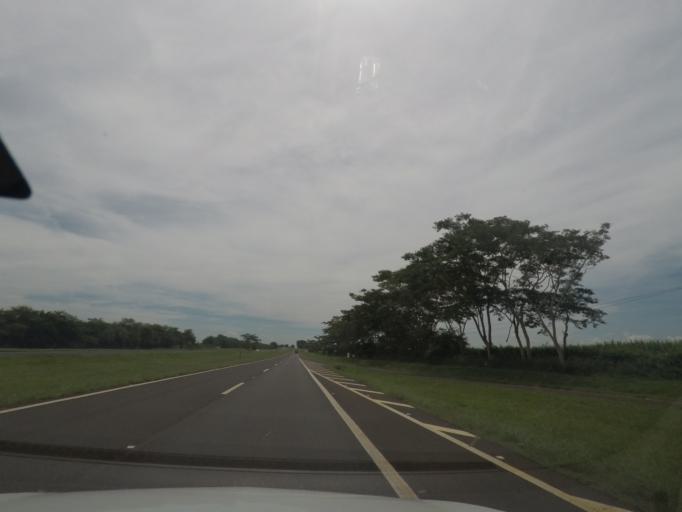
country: BR
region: Sao Paulo
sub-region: Bebedouro
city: Bebedouro
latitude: -20.9592
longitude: -48.4437
